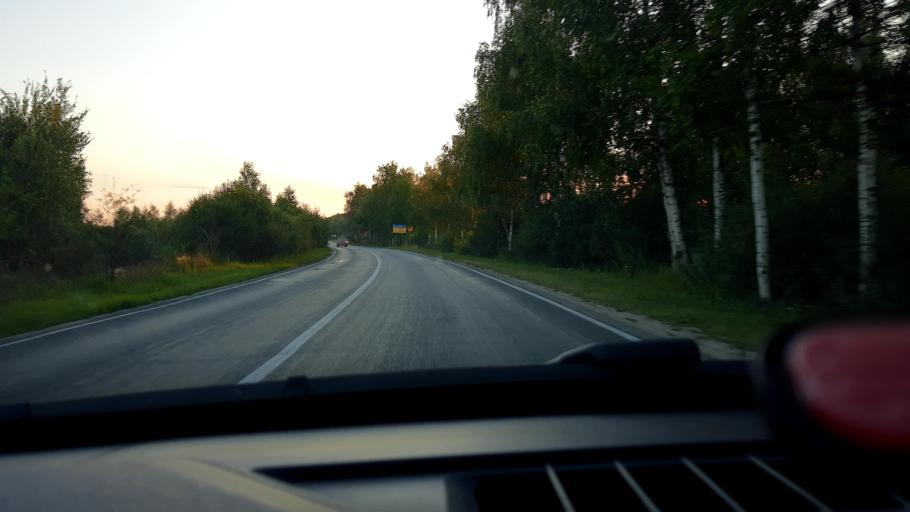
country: RU
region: Nizjnij Novgorod
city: Neklyudovo
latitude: 56.5281
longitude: 43.8370
